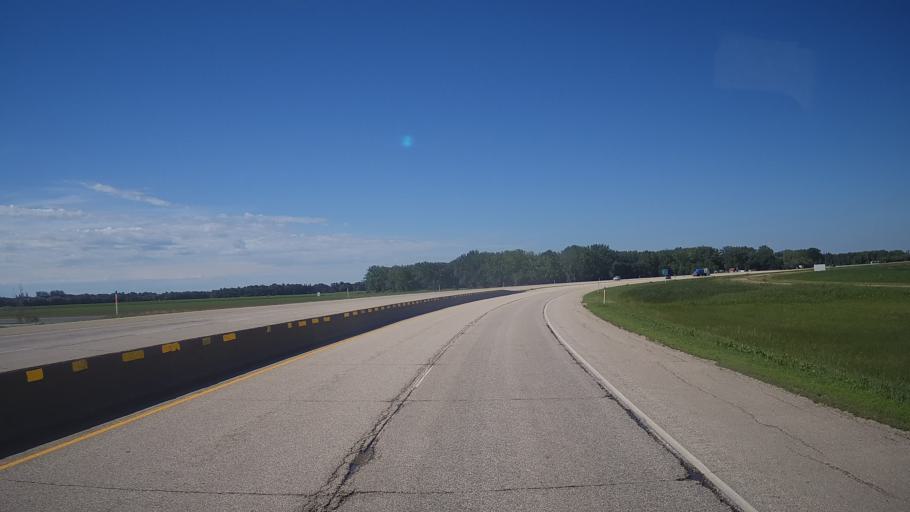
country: CA
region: Manitoba
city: Portage la Prairie
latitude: 49.9630
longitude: -98.2381
